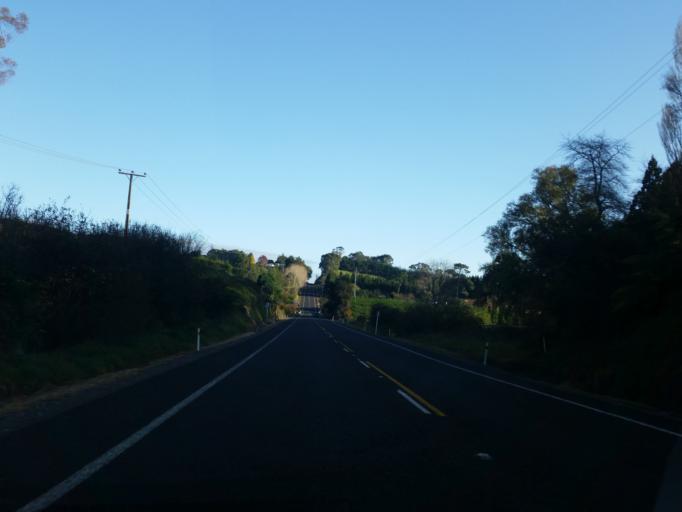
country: NZ
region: Bay of Plenty
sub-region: Western Bay of Plenty District
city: Katikati
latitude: -37.6598
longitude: 176.0061
